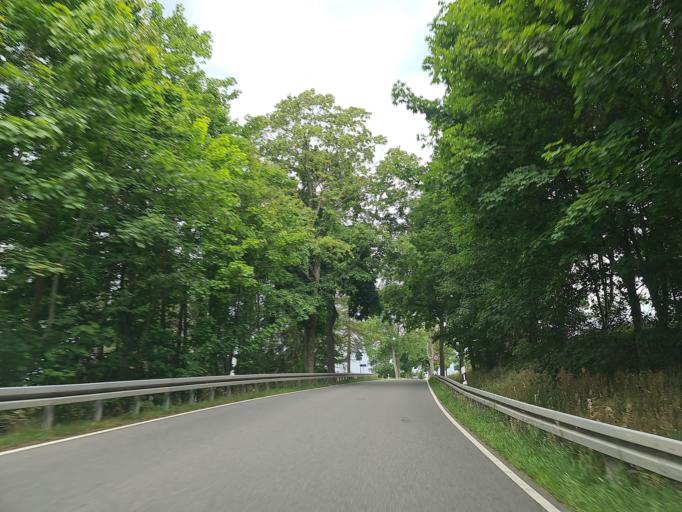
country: DE
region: Saxony
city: Pfaffroda
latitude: 50.7278
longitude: 13.3381
